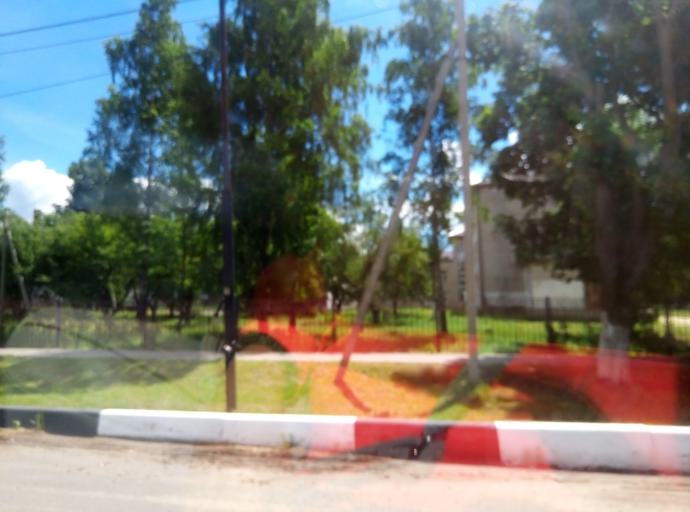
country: RU
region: Kursk
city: Oboyan'
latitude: 51.2137
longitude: 36.2878
